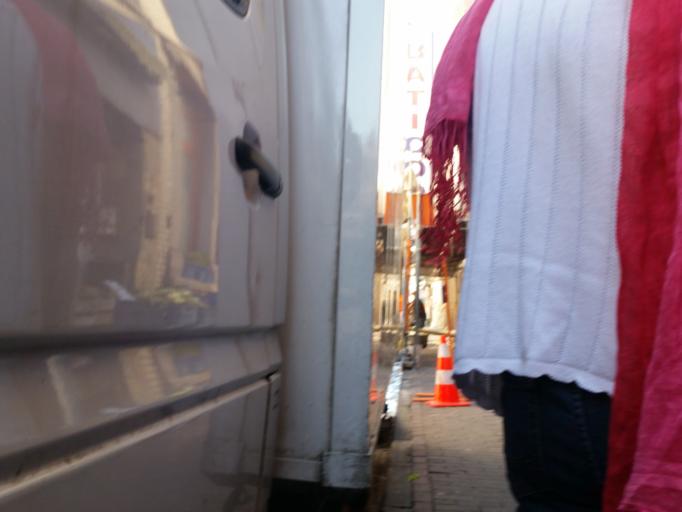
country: BE
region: Brussels Capital
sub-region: Bruxelles-Capitale
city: Brussels
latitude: 50.8310
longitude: 4.3390
